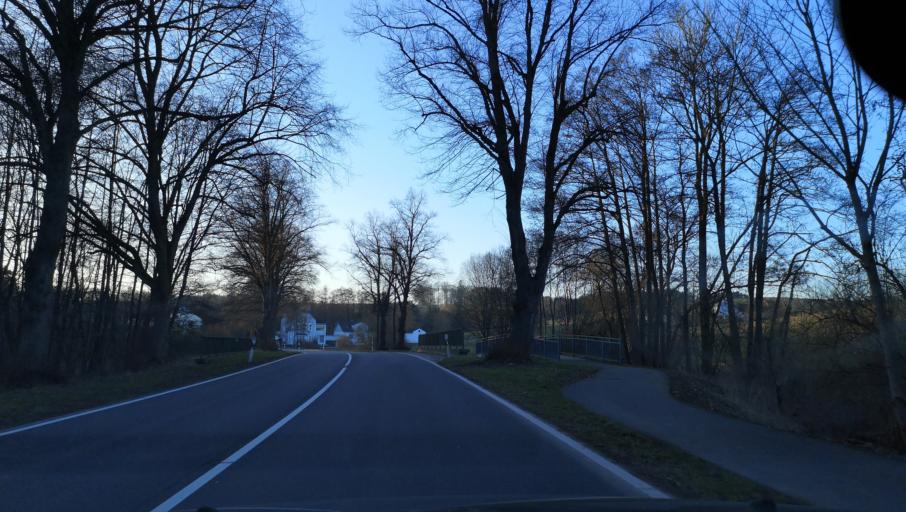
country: DE
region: North Rhine-Westphalia
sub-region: Regierungsbezirk Koln
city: Marienheide
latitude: 51.1140
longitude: 7.4833
